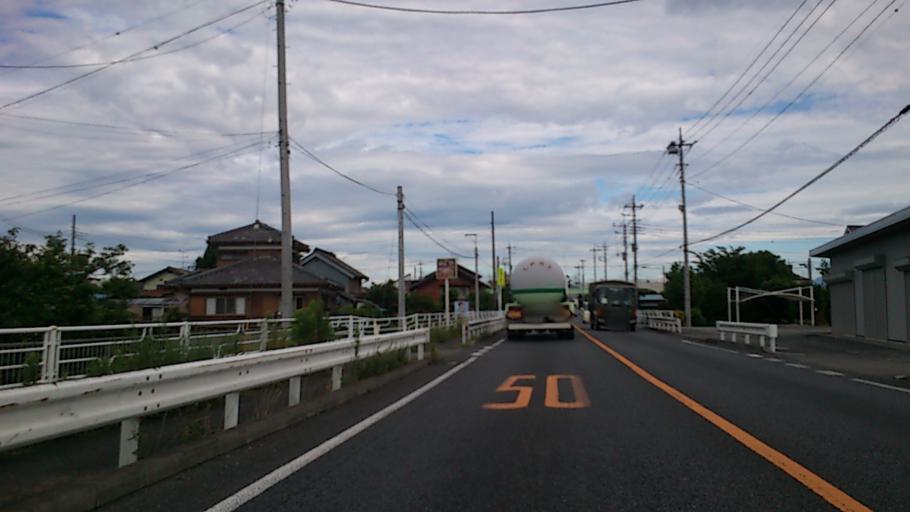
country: JP
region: Saitama
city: Honjo
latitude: 36.2576
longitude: 139.1541
